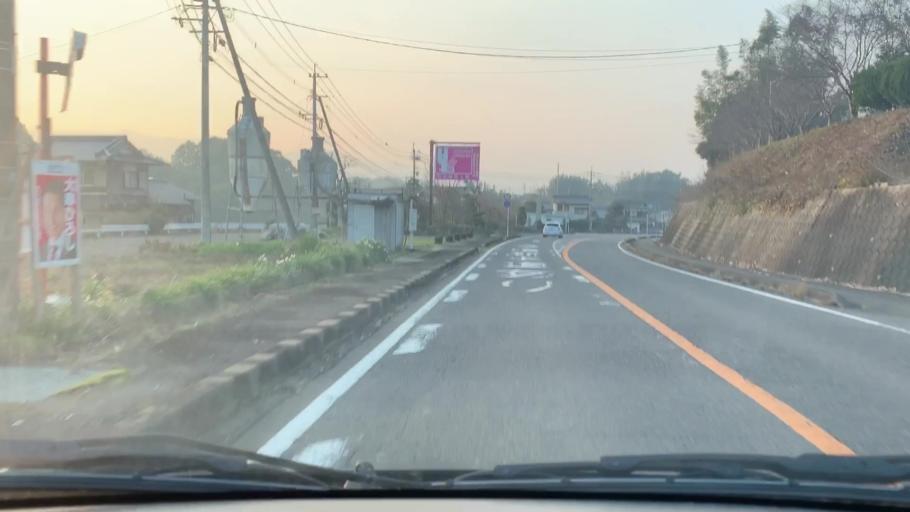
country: JP
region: Saga Prefecture
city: Imaricho-ko
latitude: 33.2653
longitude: 129.9042
